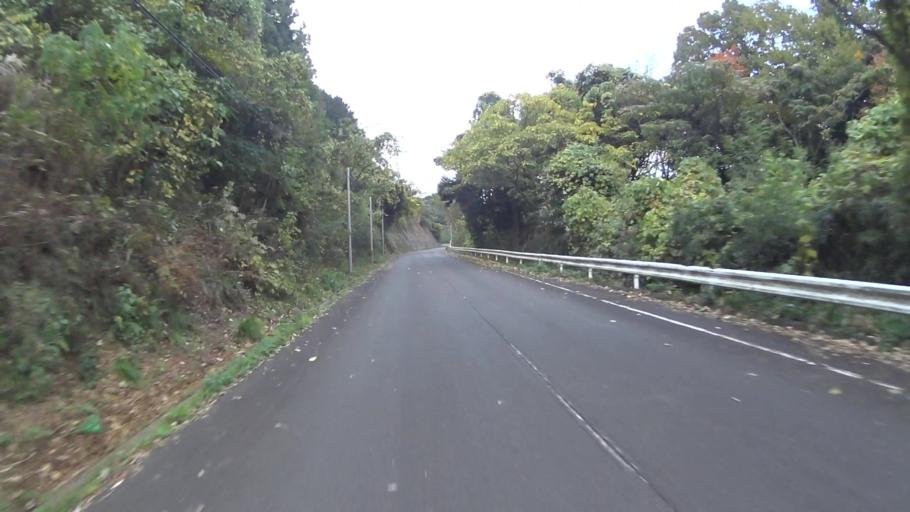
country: JP
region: Kyoto
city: Maizuru
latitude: 35.5653
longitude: 135.4623
